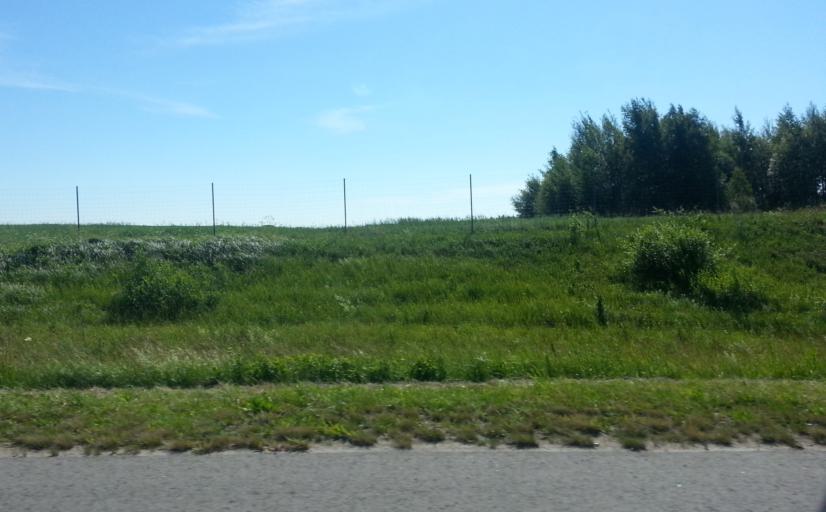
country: LT
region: Vilnius County
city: Ukmerge
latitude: 55.1910
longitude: 24.8123
